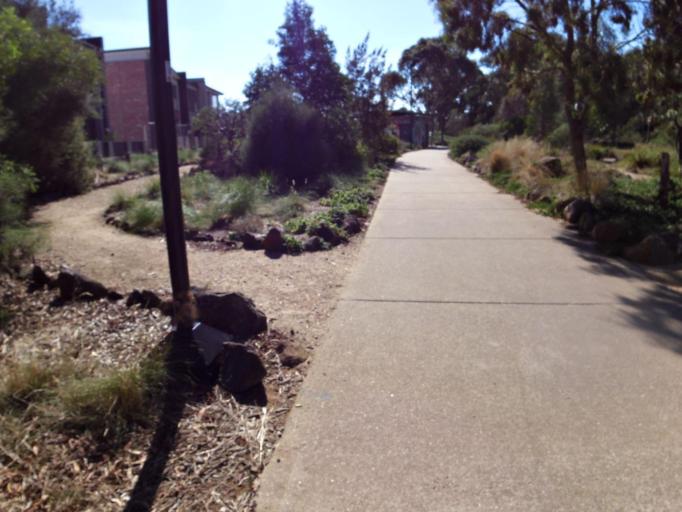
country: AU
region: Victoria
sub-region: Melton
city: Melton
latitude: -37.6919
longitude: 144.5885
